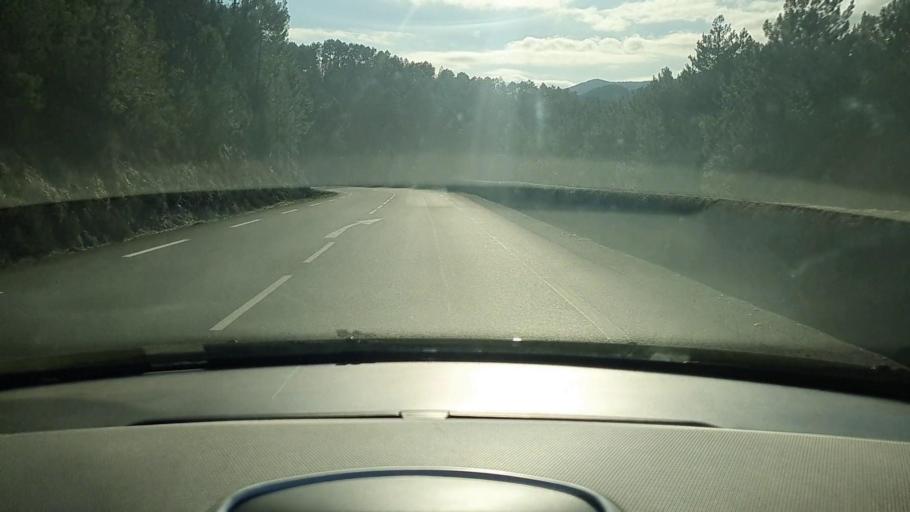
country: FR
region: Languedoc-Roussillon
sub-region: Departement du Gard
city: Branoux-les-Taillades
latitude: 44.3276
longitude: 3.9676
